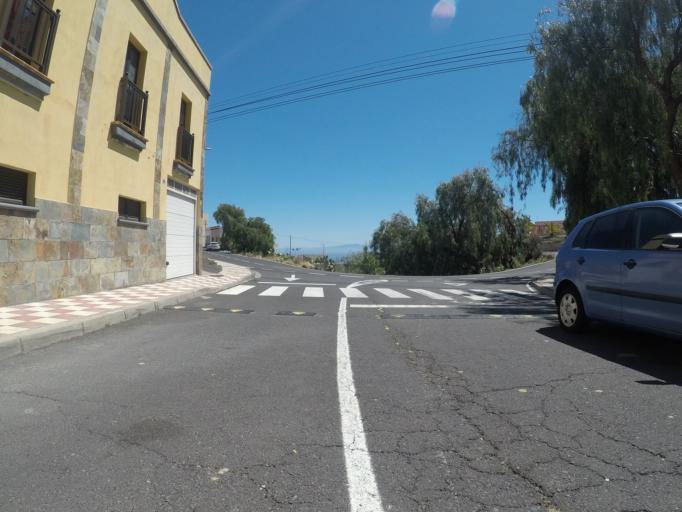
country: ES
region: Canary Islands
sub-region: Provincia de Santa Cruz de Tenerife
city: Lomo de Arico
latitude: 28.1816
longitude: -16.4814
